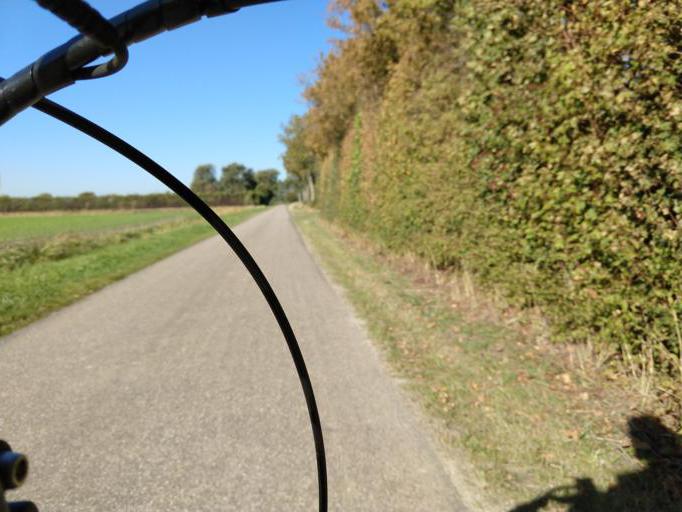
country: NL
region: Zeeland
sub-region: Gemeente Terneuzen
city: Terneuzen
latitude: 51.3995
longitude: 3.8265
